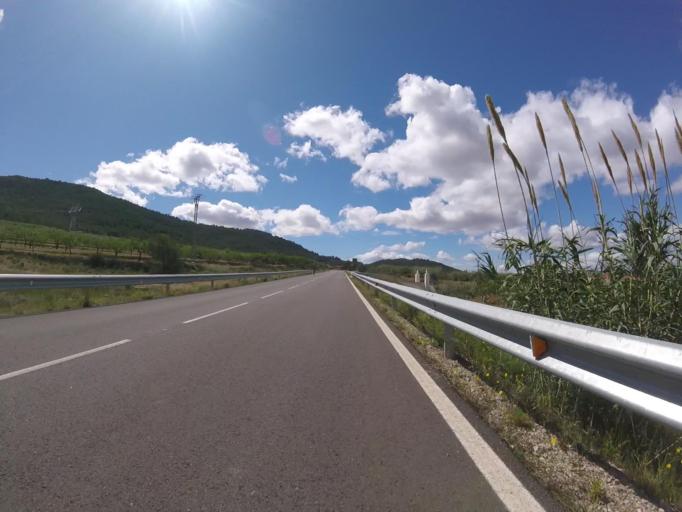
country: ES
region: Valencia
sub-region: Provincia de Castello
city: Culla
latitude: 40.2865
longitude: -0.1134
